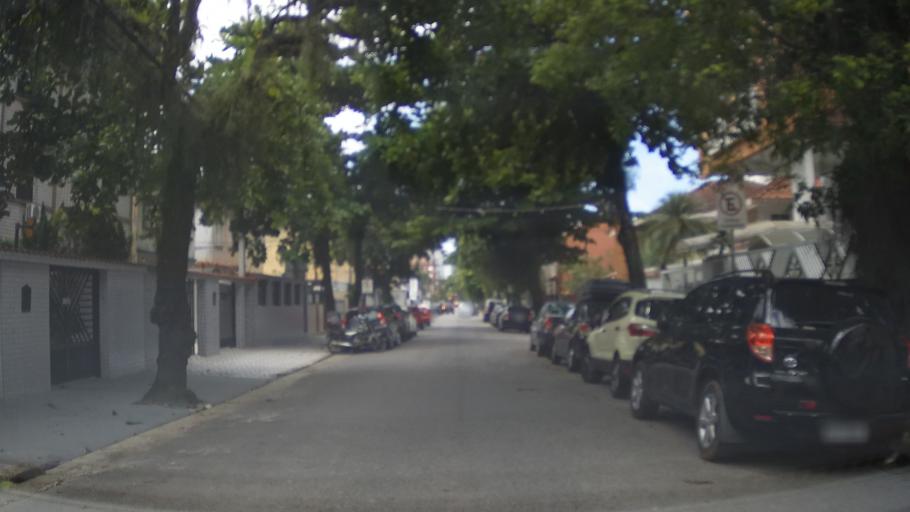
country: BR
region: Sao Paulo
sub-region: Santos
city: Santos
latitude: -23.9613
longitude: -46.3483
